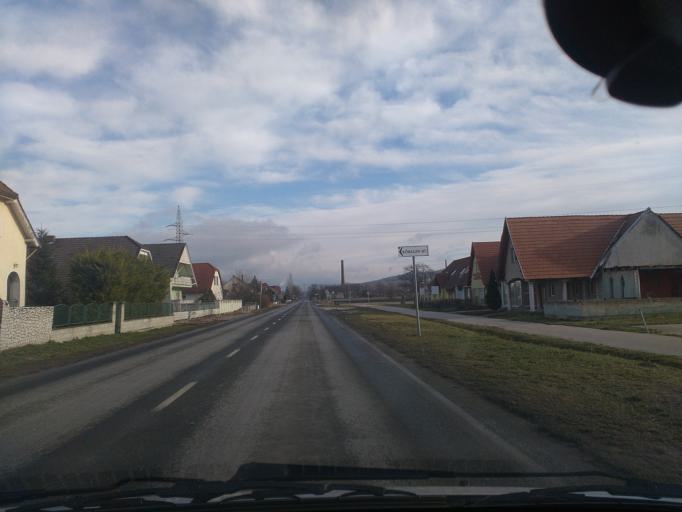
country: HU
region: Komarom-Esztergom
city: Tat
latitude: 47.7381
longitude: 18.6624
